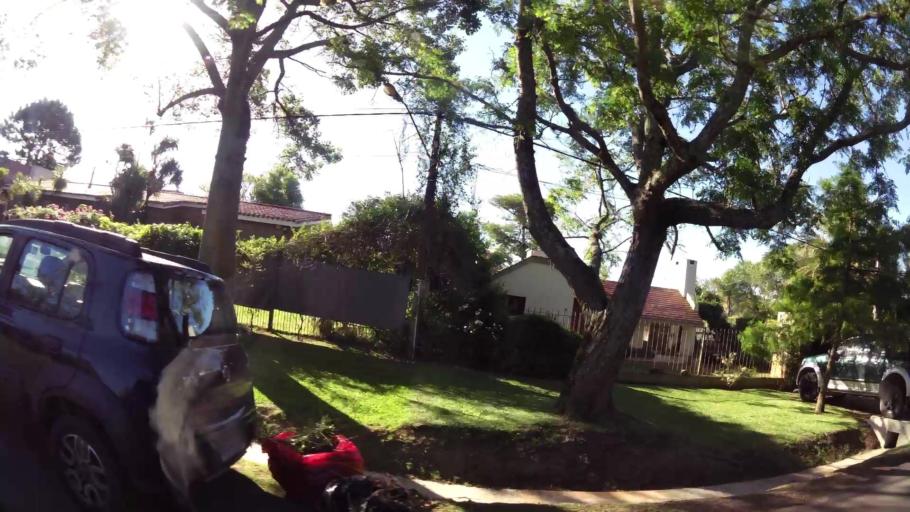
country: UY
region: Canelones
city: Barra de Carrasco
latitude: -34.8615
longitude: -56.0326
